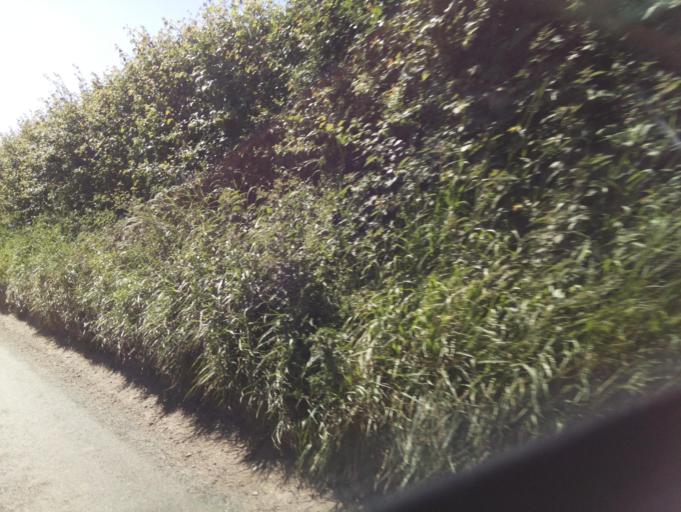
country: GB
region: England
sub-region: Somerset
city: Merriott
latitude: 50.8973
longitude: -2.7623
